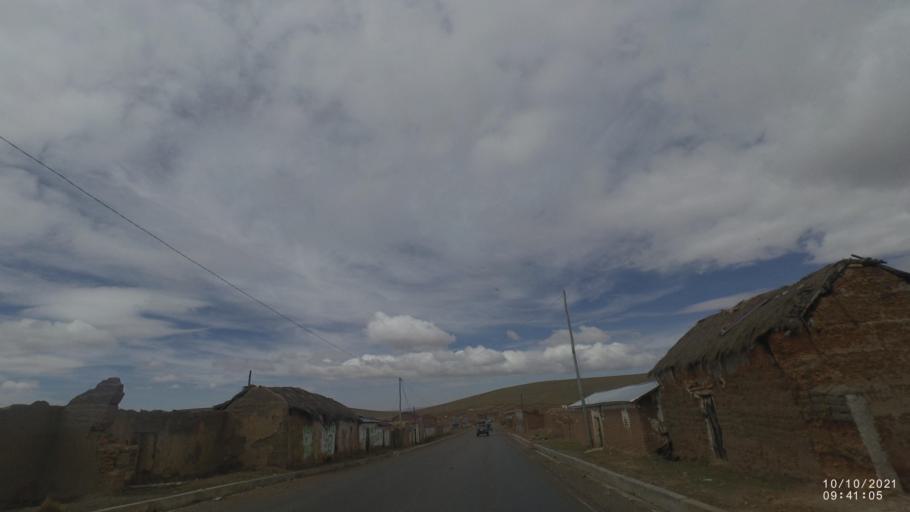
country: BO
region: La Paz
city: Quime
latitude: -17.1446
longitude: -67.3432
